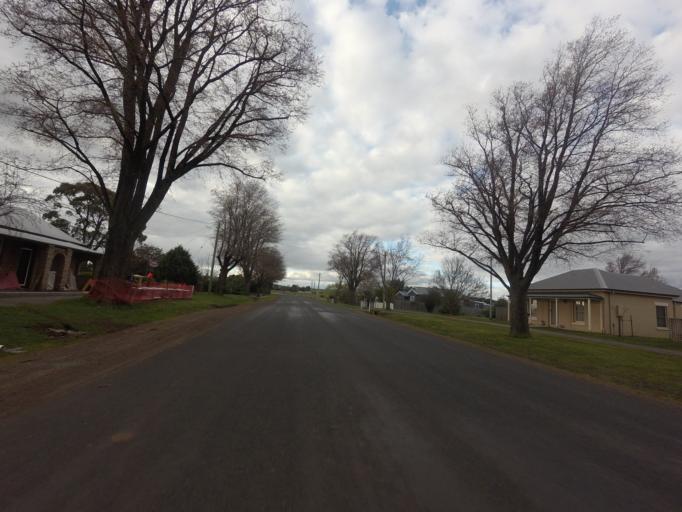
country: AU
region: Tasmania
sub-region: Northern Midlands
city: Evandale
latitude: -42.0267
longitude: 147.4932
